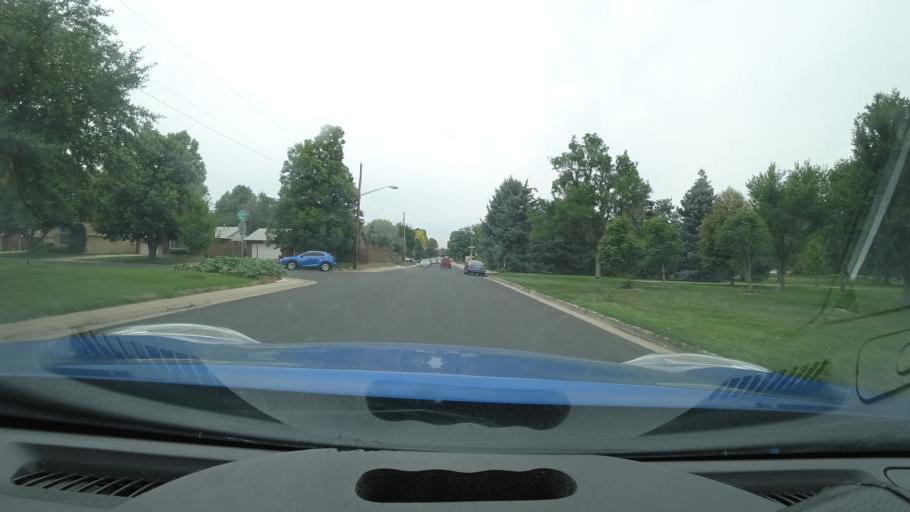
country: US
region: Colorado
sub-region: Arapahoe County
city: Glendale
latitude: 39.6858
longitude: -104.9113
